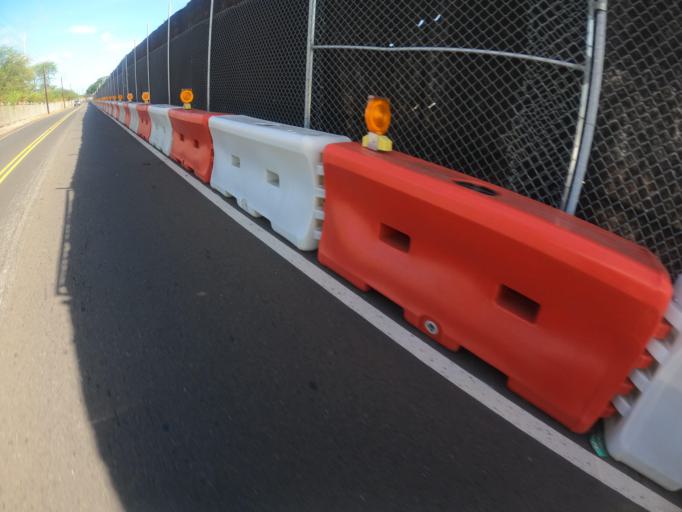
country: US
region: Hawaii
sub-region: Honolulu County
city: Makakilo City
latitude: 21.3246
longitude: -158.0835
